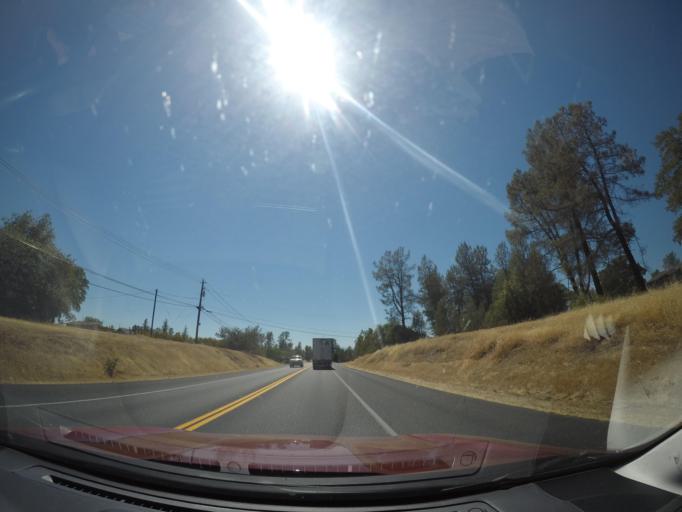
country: US
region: California
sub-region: Shasta County
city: Bella Vista
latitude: 40.6289
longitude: -122.2814
